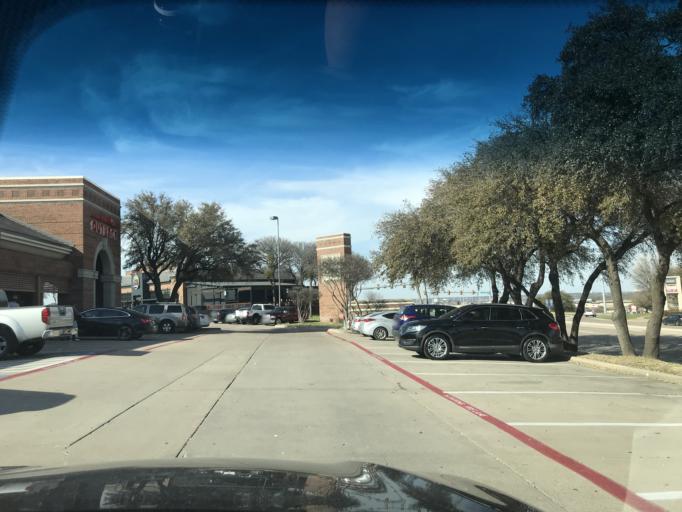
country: US
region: Texas
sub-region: Tarrant County
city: Benbrook
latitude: 32.6812
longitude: -97.4144
